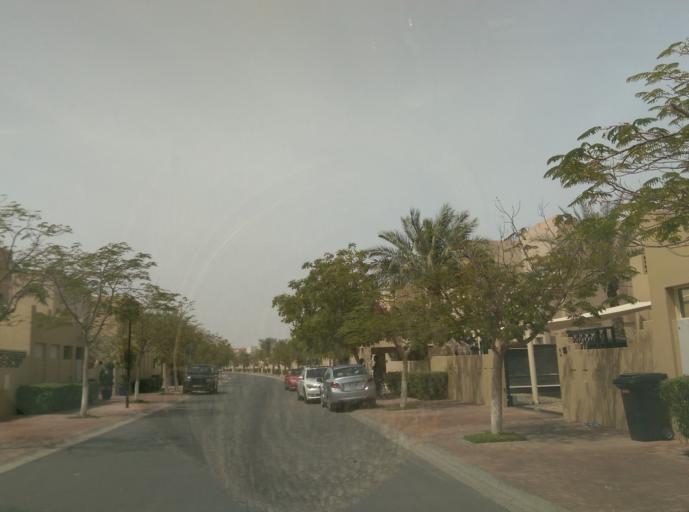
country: AE
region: Dubai
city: Dubai
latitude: 25.0633
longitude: 55.1787
